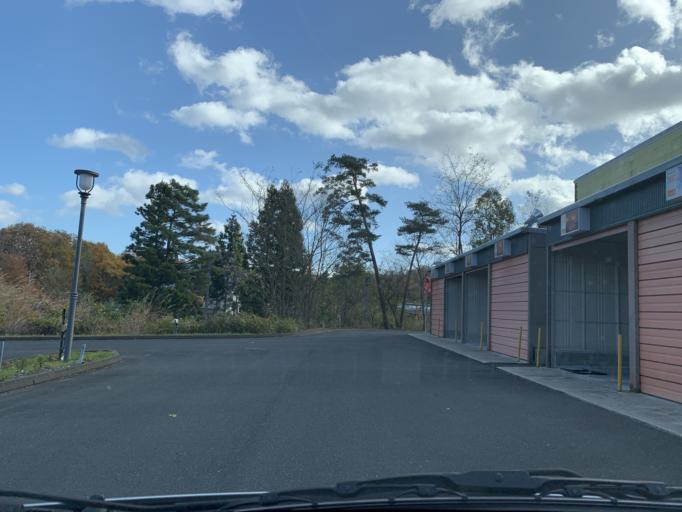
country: JP
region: Iwate
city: Mizusawa
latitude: 39.0421
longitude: 141.1014
